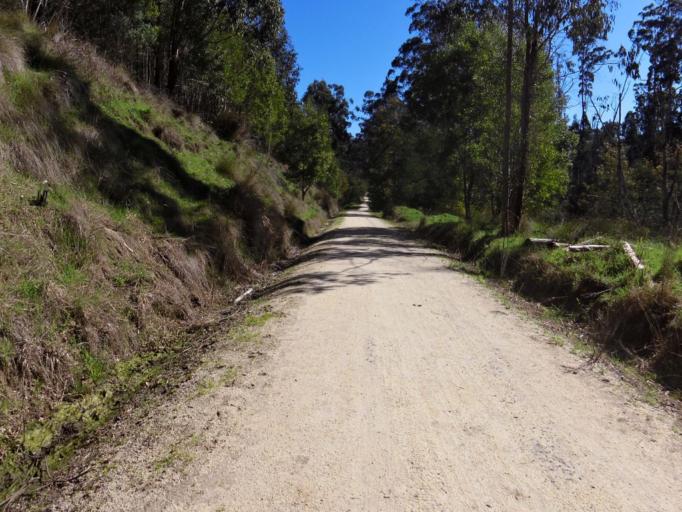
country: AU
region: Victoria
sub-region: Latrobe
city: Moe
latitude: -38.3844
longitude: 146.2516
